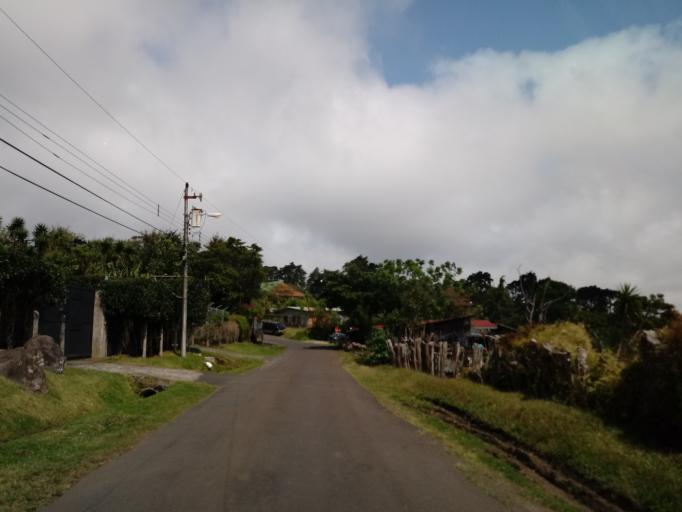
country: CR
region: Heredia
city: Angeles
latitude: 10.0301
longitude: -84.0324
